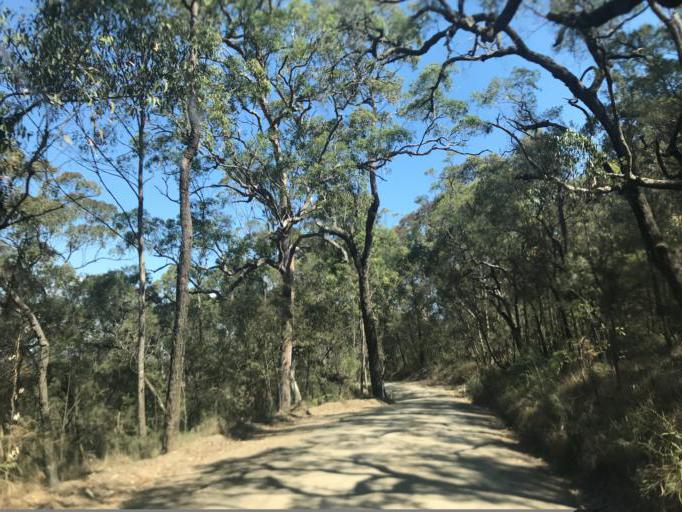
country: AU
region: New South Wales
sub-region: Hawkesbury
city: Pitt Town
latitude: -33.4090
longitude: 150.9238
